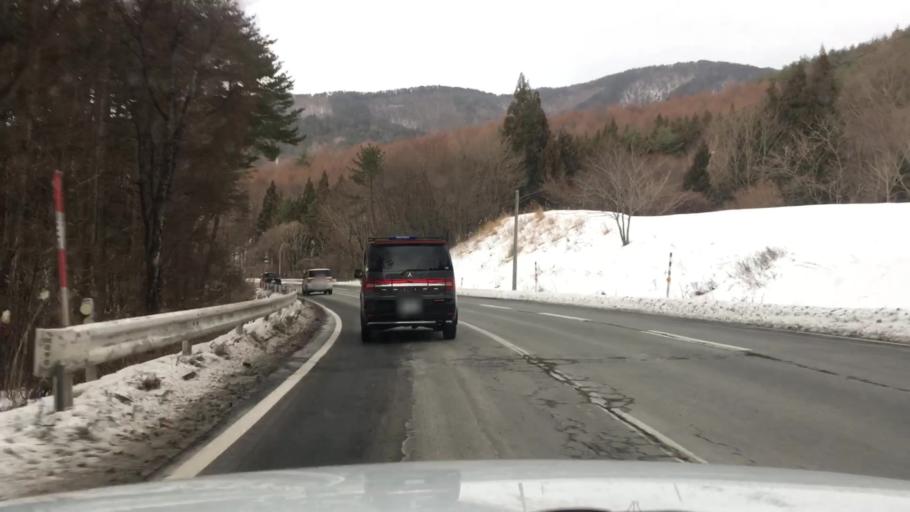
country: JP
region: Iwate
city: Morioka-shi
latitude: 39.6665
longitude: 141.3322
